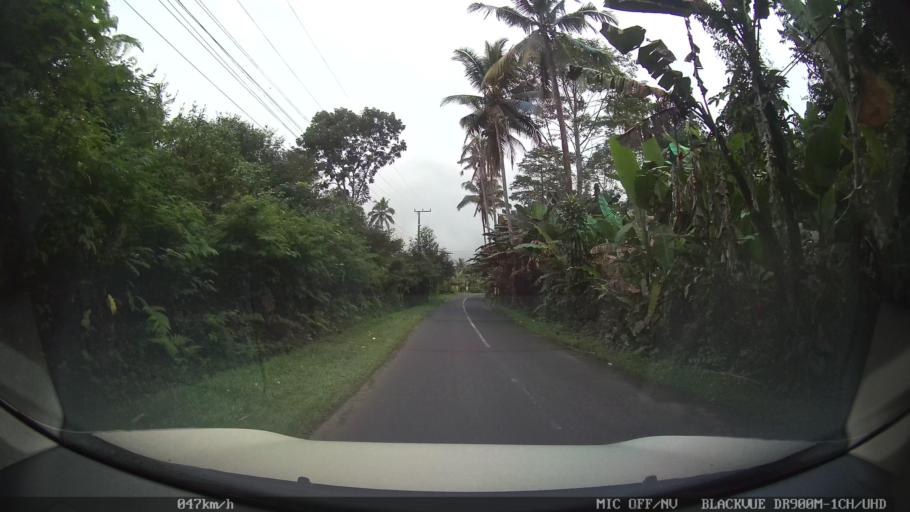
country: ID
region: Bali
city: Peneng
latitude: -8.3707
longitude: 115.1768
